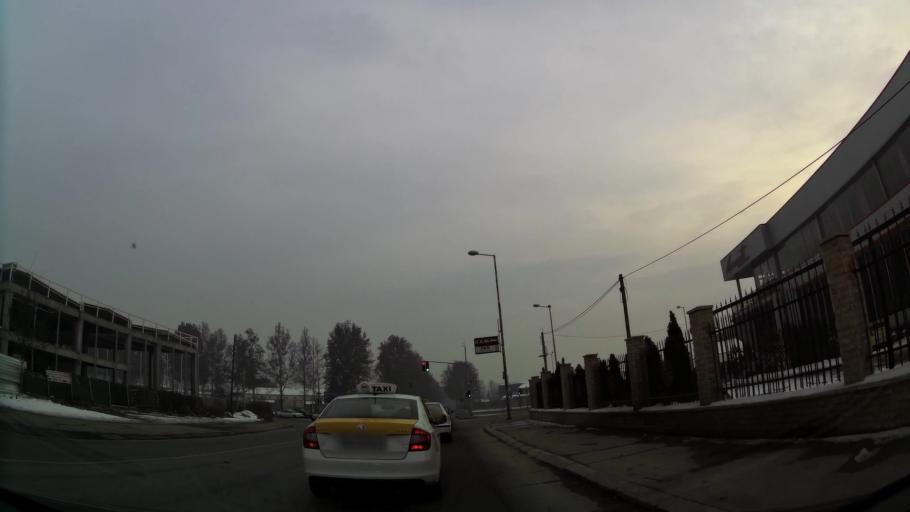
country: MK
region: Suto Orizari
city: Suto Orizare
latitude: 42.0260
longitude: 21.4296
